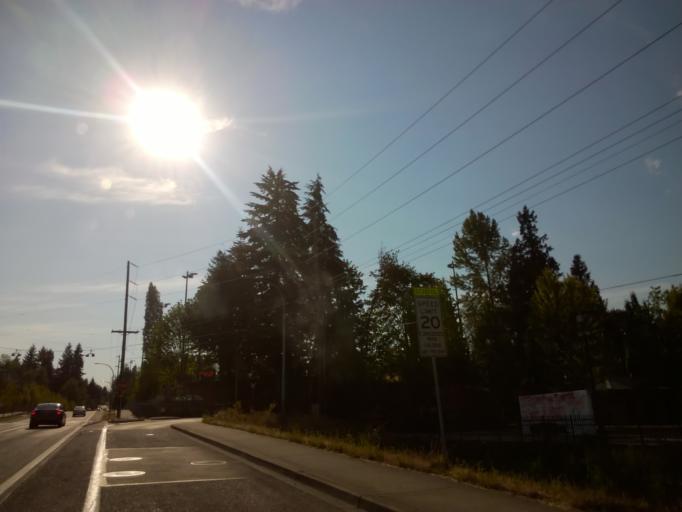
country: US
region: Washington
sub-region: King County
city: Woodinville
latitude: 47.7690
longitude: -122.1584
